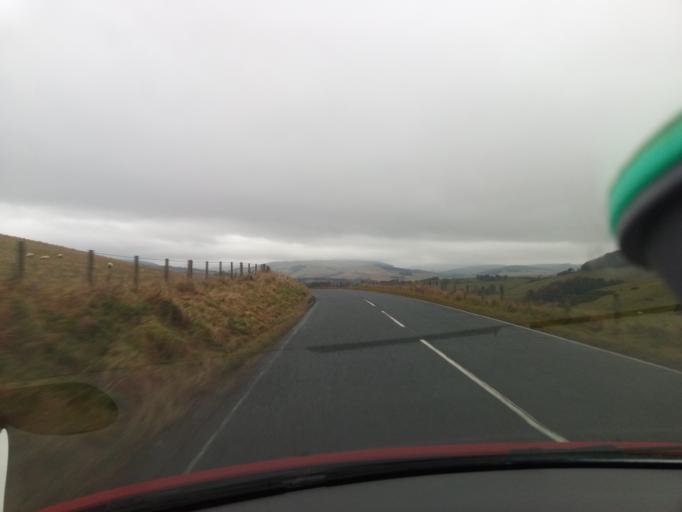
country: GB
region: Scotland
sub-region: The Scottish Borders
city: Selkirk
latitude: 55.5408
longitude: -2.8163
